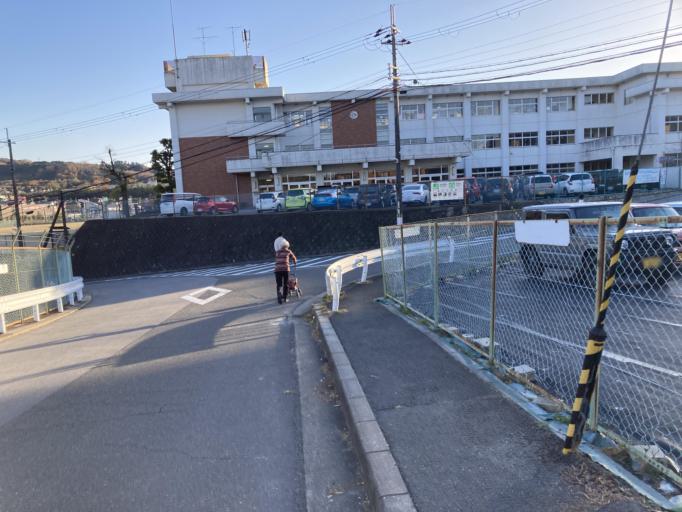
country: JP
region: Nara
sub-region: Ikoma-shi
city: Ikoma
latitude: 34.6730
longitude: 135.7155
